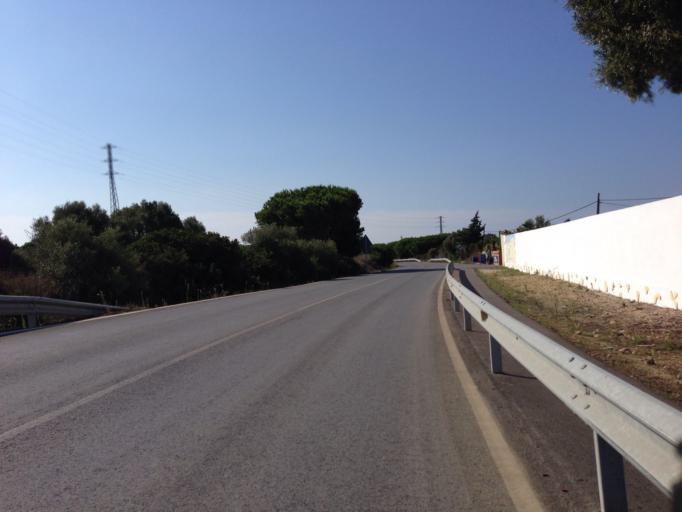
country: ES
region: Andalusia
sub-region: Provincia de Cadiz
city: Vejer de la Frontera
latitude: 36.1972
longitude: -6.0306
